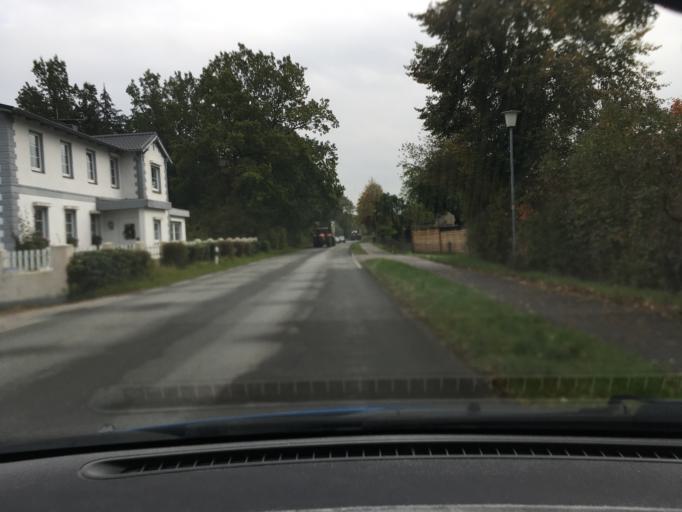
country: DE
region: Schleswig-Holstein
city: Klein Ronnau
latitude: 53.9685
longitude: 10.3165
